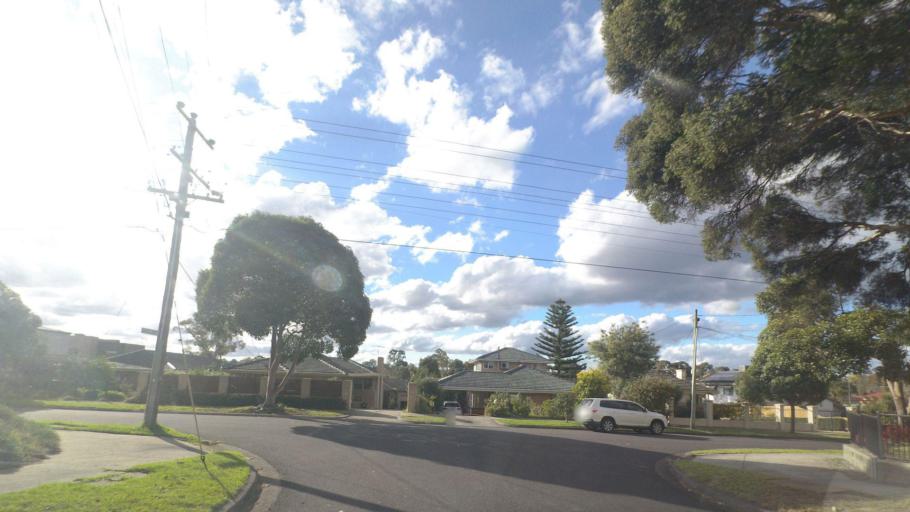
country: AU
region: Victoria
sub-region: Manningham
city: Doncaster East
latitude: -37.7845
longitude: 145.1518
